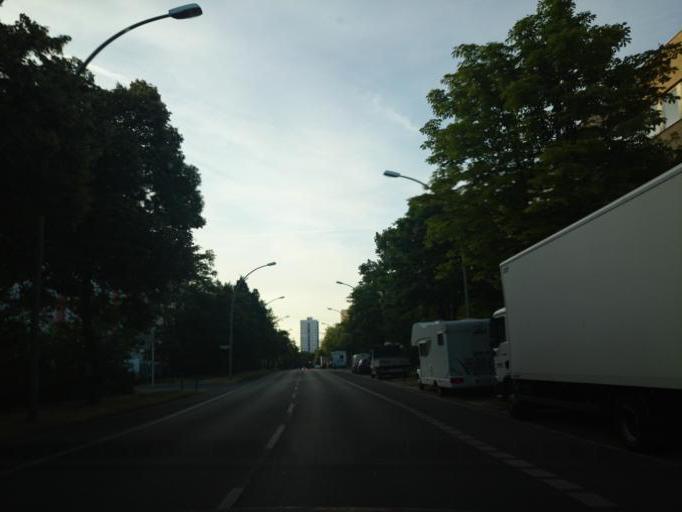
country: DE
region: Berlin
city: Fennpfuhl
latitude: 52.5303
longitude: 13.4855
